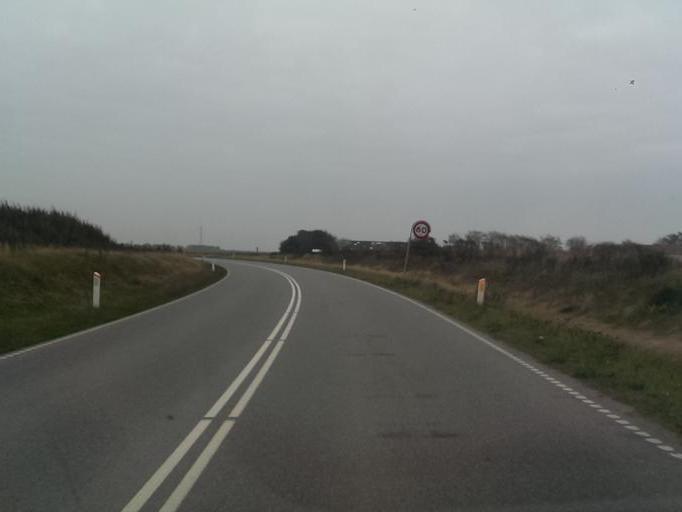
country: DK
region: South Denmark
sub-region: Esbjerg Kommune
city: Tjaereborg
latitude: 55.4651
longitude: 8.5560
